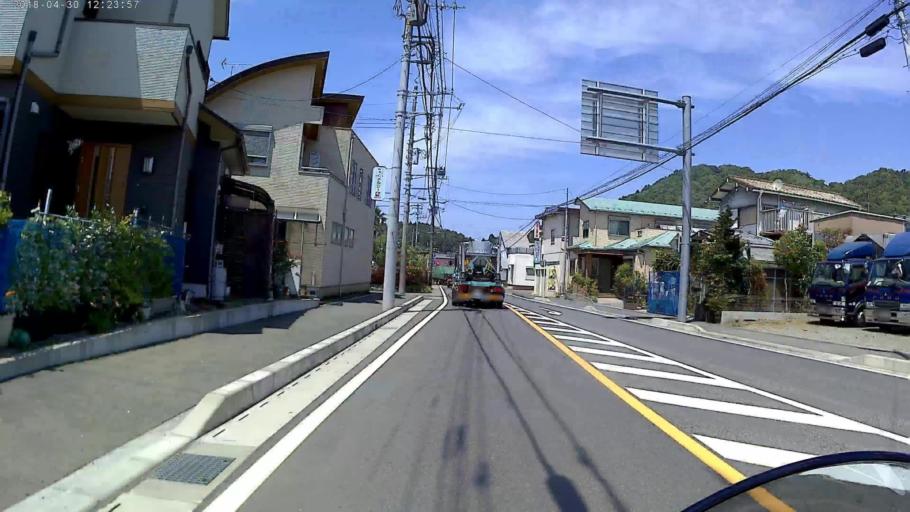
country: JP
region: Tokyo
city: Hachioji
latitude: 35.5751
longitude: 139.2754
